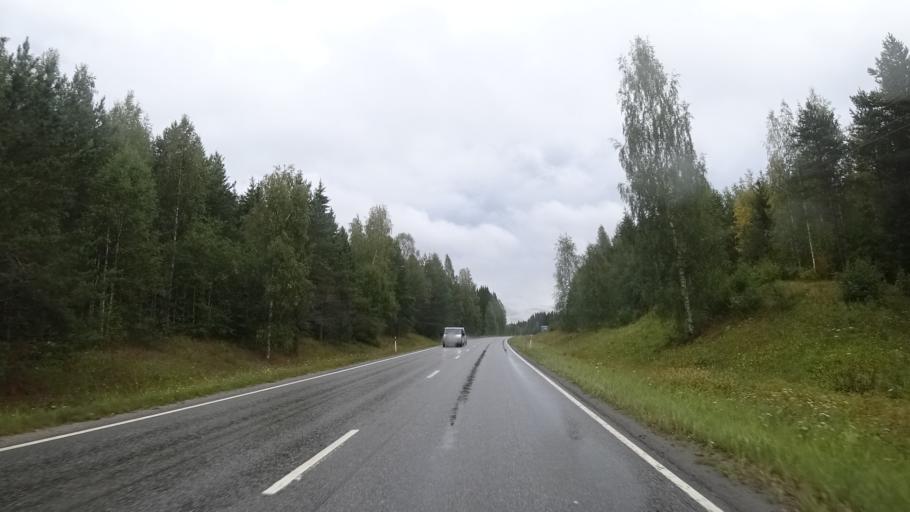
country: FI
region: Southern Savonia
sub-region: Savonlinna
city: Kerimaeki
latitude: 61.9844
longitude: 29.2797
